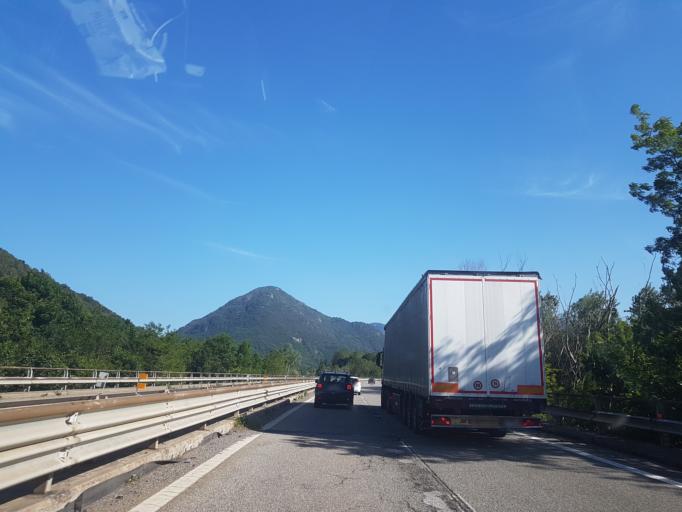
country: IT
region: Piedmont
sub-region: Provincia Verbano-Cusio-Ossola
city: Ornavasso
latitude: 45.9720
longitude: 8.4260
